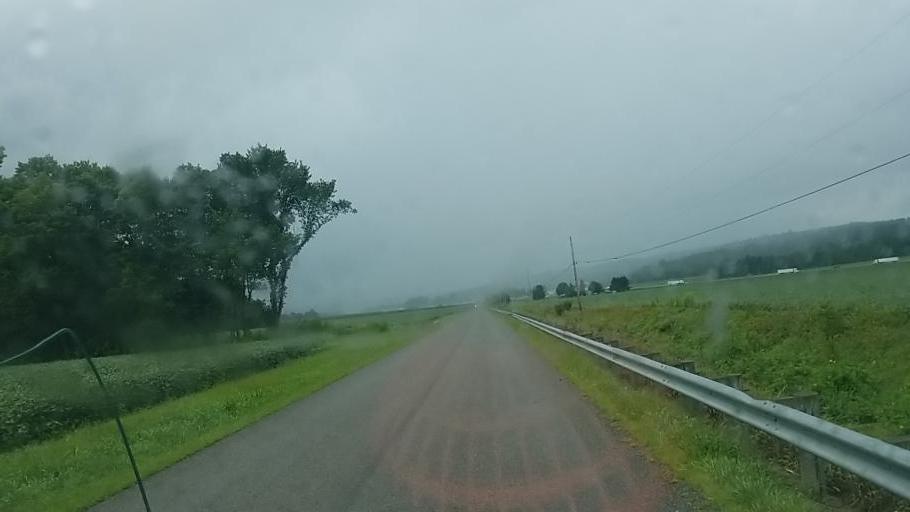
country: US
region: Ohio
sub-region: Logan County
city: Bellefontaine
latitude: 40.3204
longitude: -83.6393
